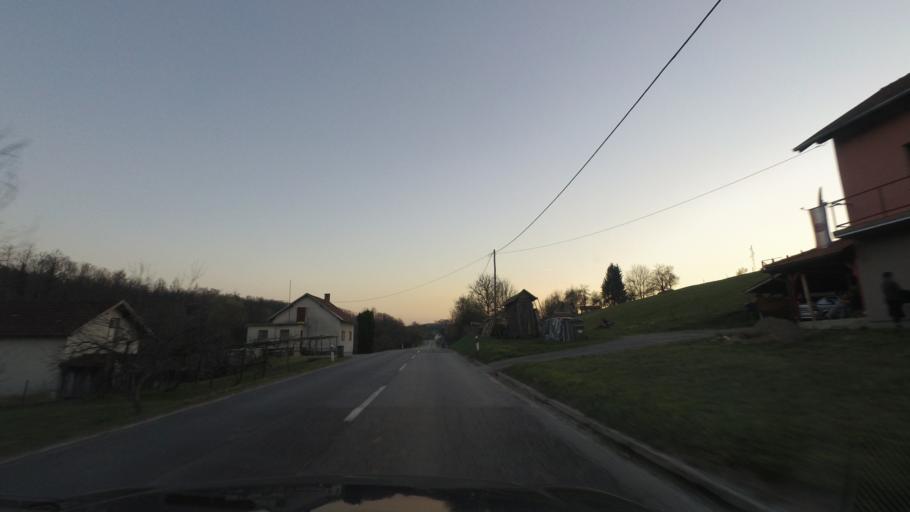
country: HR
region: Karlovacka
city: Vojnic
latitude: 45.3287
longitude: 15.7115
